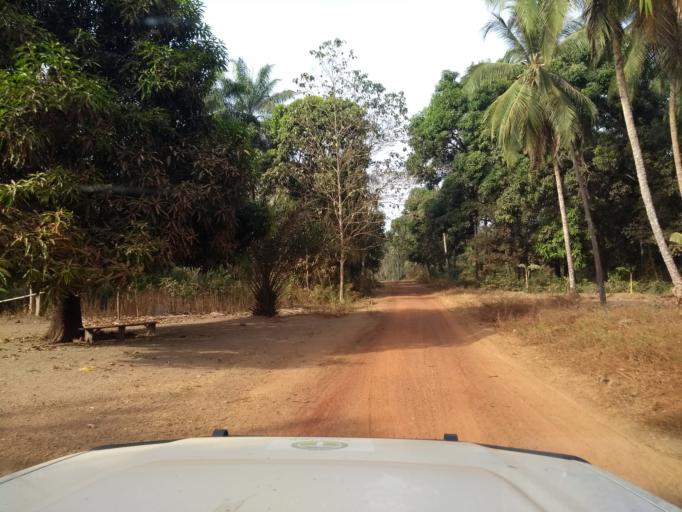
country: GN
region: Kindia
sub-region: Prefecture de Dubreka
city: Dubreka
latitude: 9.8609
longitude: -13.5465
